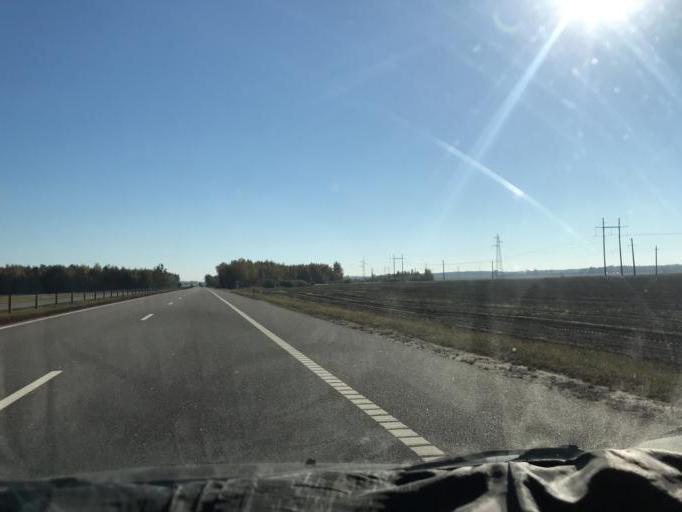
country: BY
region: Mogilev
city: Yalizava
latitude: 53.2280
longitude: 28.9978
